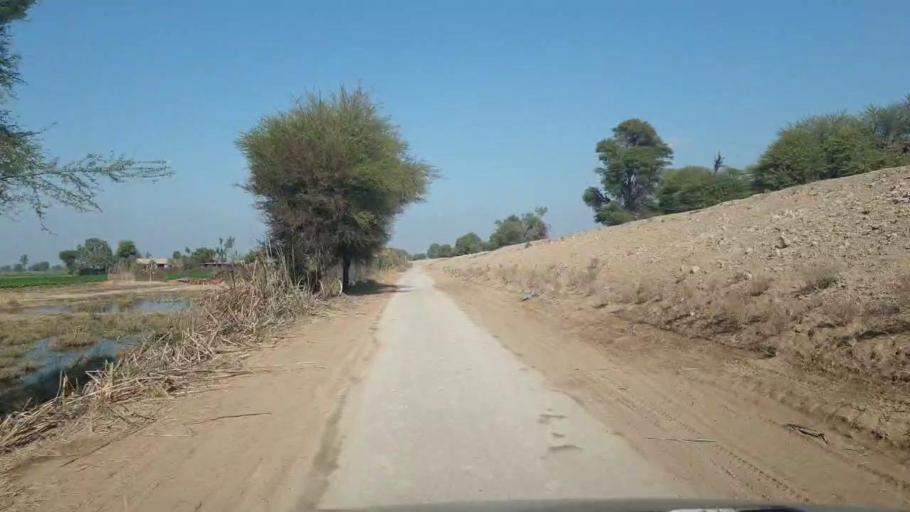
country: PK
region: Sindh
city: Shahdadpur
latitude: 25.8786
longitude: 68.5467
